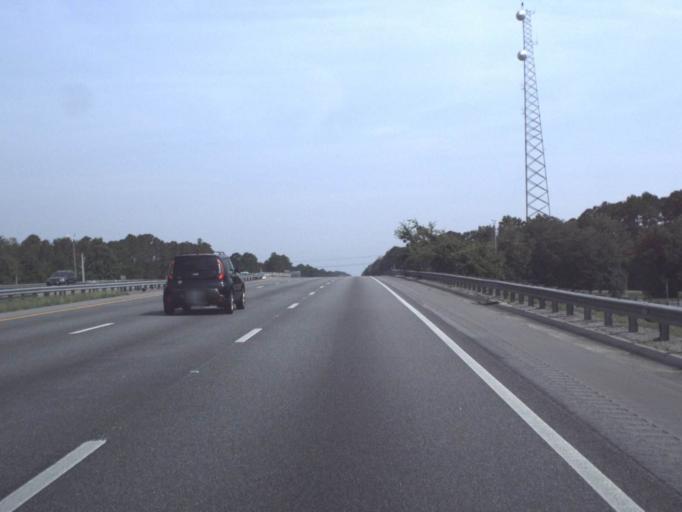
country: US
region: Florida
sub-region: Nassau County
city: Yulee
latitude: 30.6181
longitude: -81.6493
